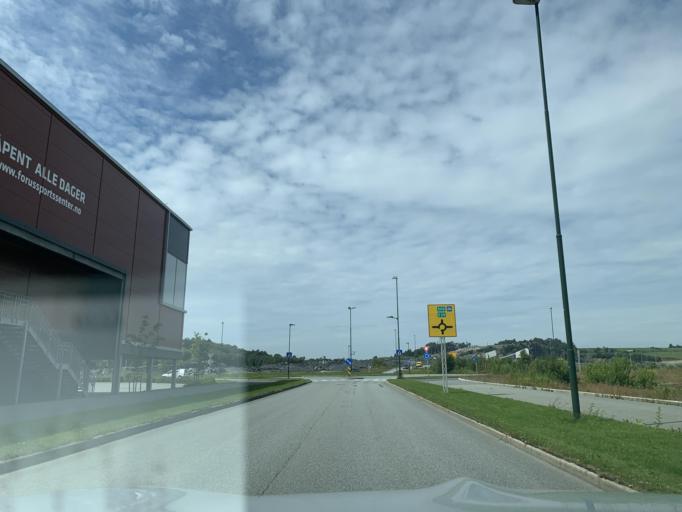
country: NO
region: Rogaland
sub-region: Sola
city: Sola
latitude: 58.8944
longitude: 5.6809
